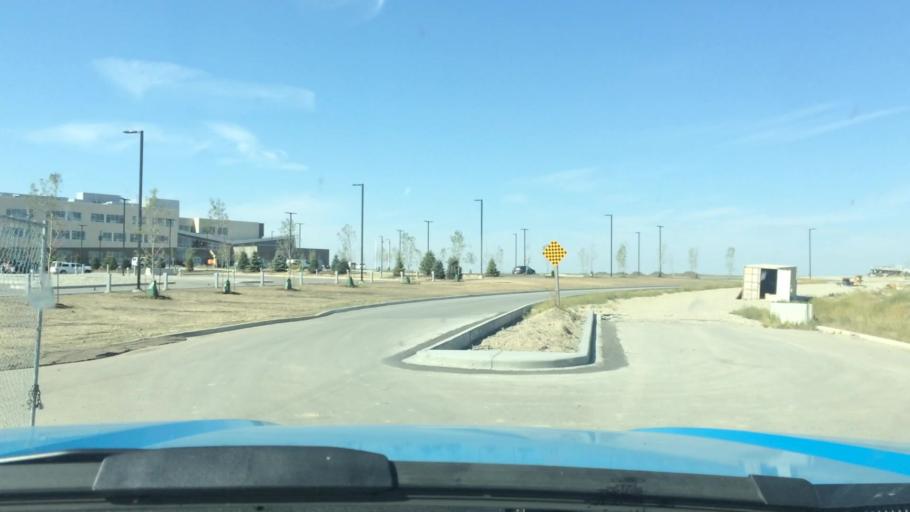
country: CA
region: Alberta
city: Airdrie
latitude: 51.2172
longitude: -113.9375
